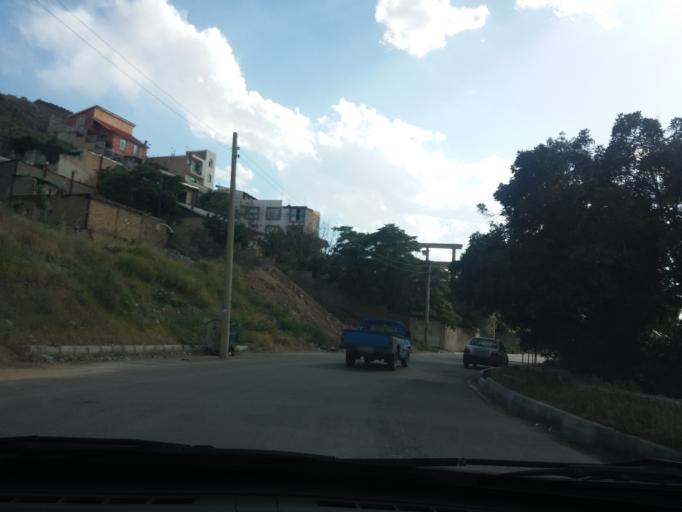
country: IR
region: Tehran
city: Damavand
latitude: 35.7279
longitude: 51.9050
